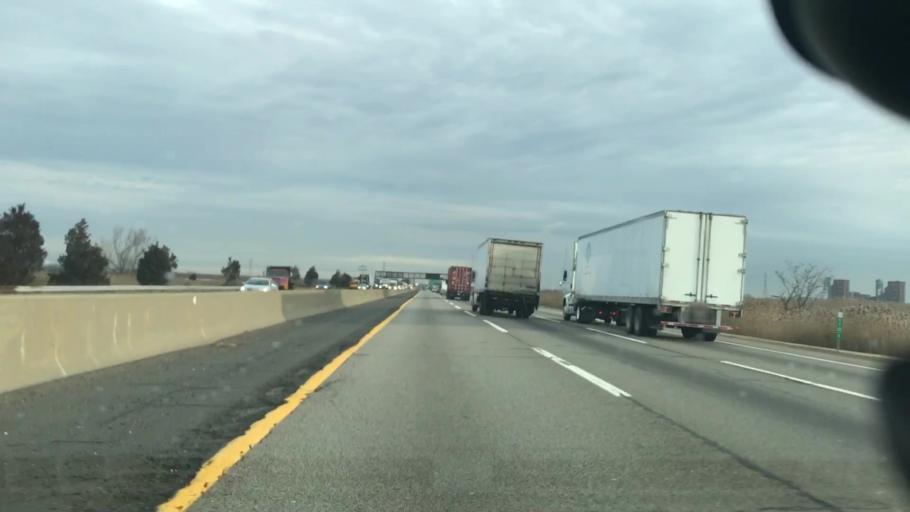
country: US
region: New Jersey
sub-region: Bergen County
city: North Arlington
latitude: 40.7711
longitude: -74.1057
